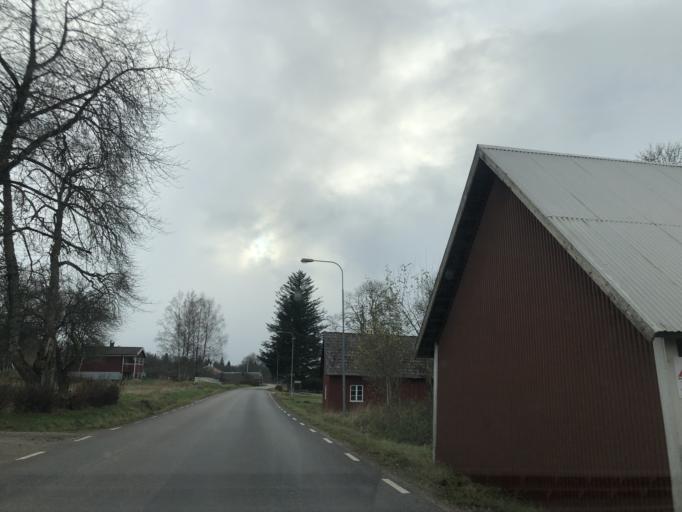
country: SE
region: Vaestra Goetaland
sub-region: Ulricehamns Kommun
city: Ulricehamn
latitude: 57.6847
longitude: 13.4161
